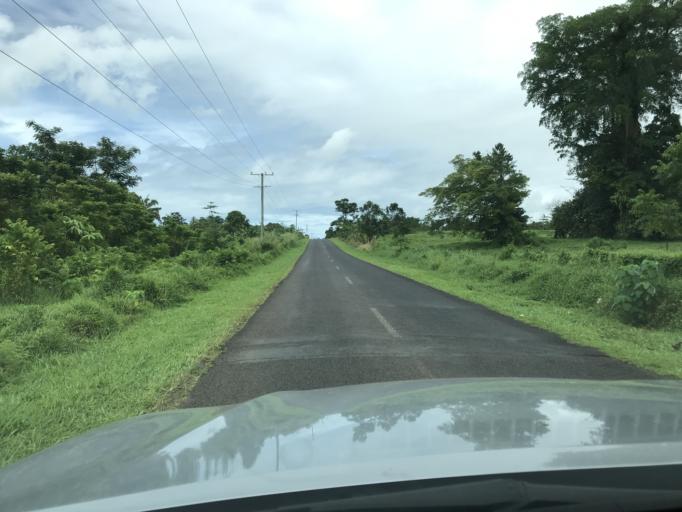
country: WS
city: Nofoali`i
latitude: -13.8759
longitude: -171.9331
